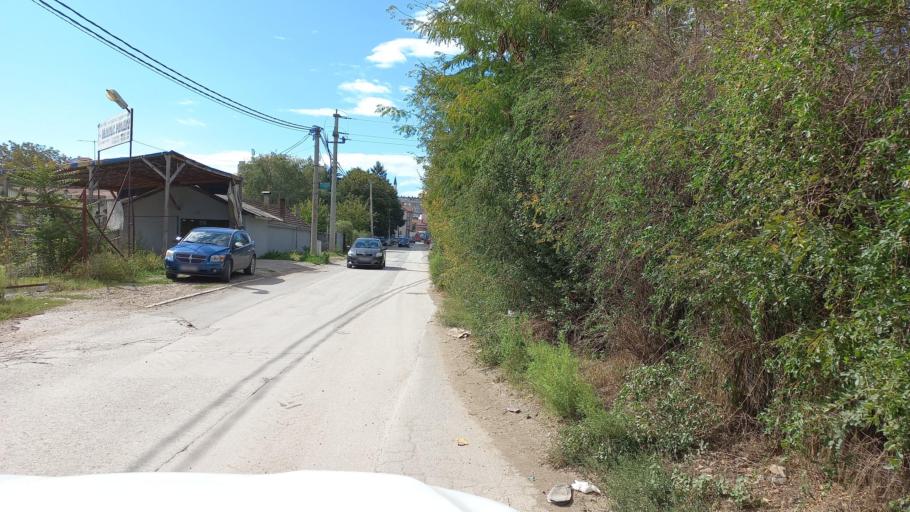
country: MK
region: Kumanovo
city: Kumanovo
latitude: 42.1406
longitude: 21.7156
